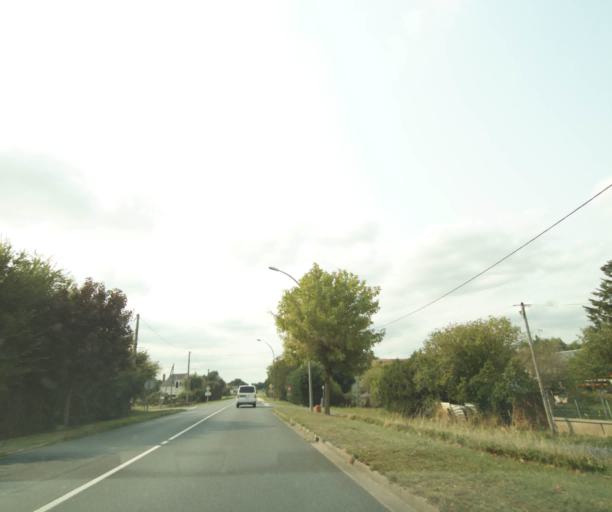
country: FR
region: Centre
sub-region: Departement de l'Indre
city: Chatillon-sur-Indre
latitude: 46.9967
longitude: 1.1570
